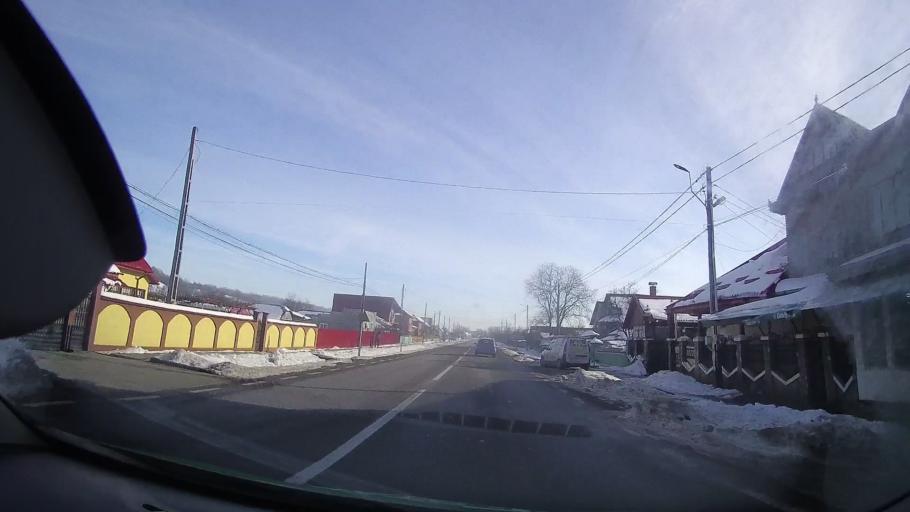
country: RO
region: Neamt
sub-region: Comuna Cracaoani
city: Cracaoani
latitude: 47.0936
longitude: 26.3188
